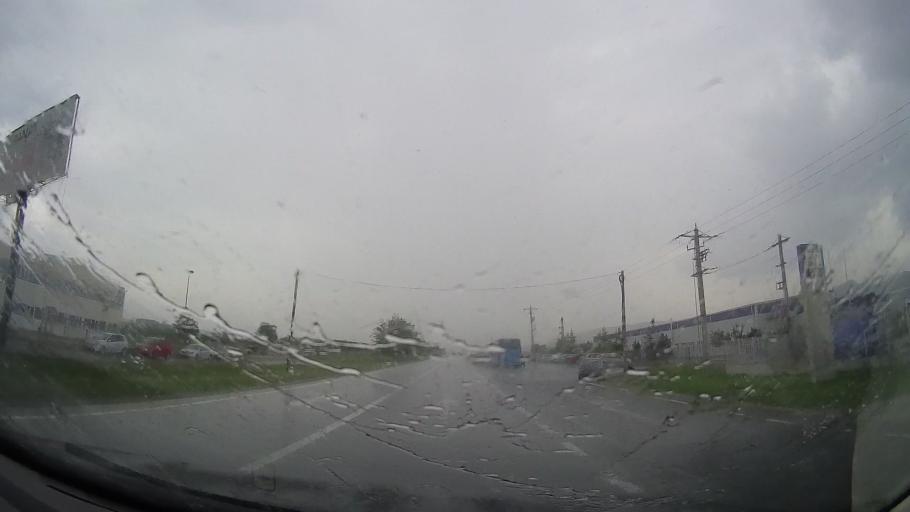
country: RO
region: Caras-Severin
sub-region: Comuna Buchin
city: Buchin
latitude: 45.3799
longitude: 22.2332
